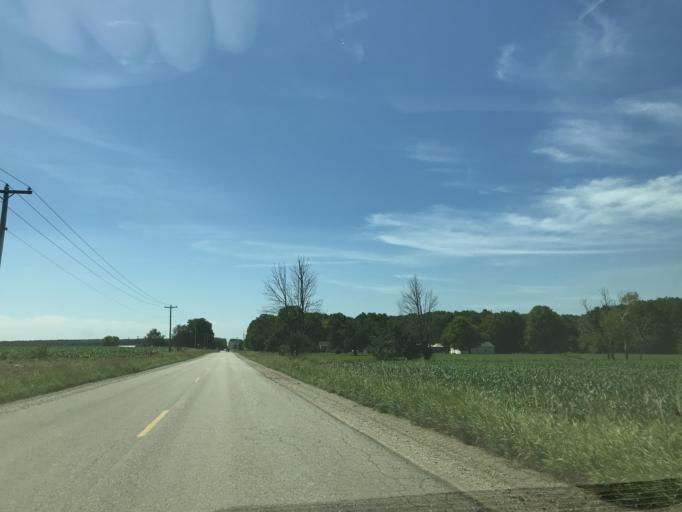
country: US
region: Michigan
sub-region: Missaukee County
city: Lake City
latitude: 44.3273
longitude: -85.0750
